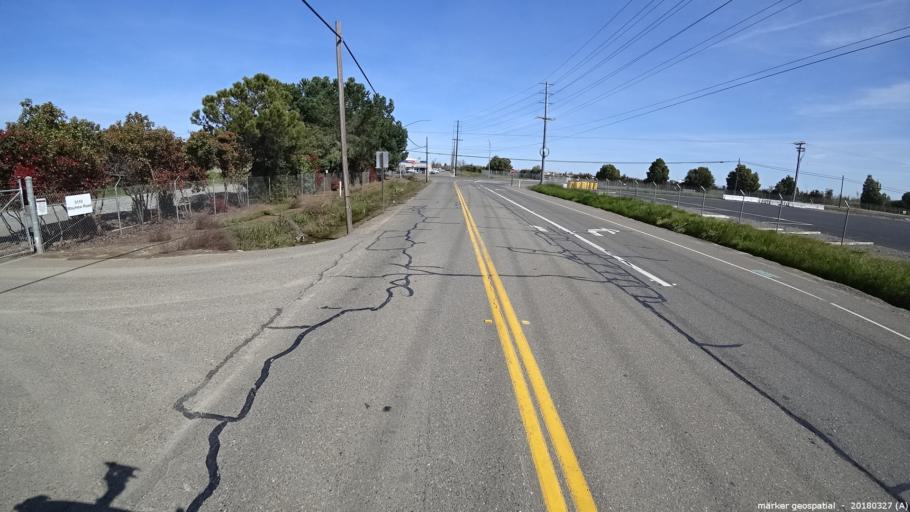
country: US
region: California
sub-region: Sacramento County
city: Rosemont
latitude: 38.5306
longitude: -121.3443
